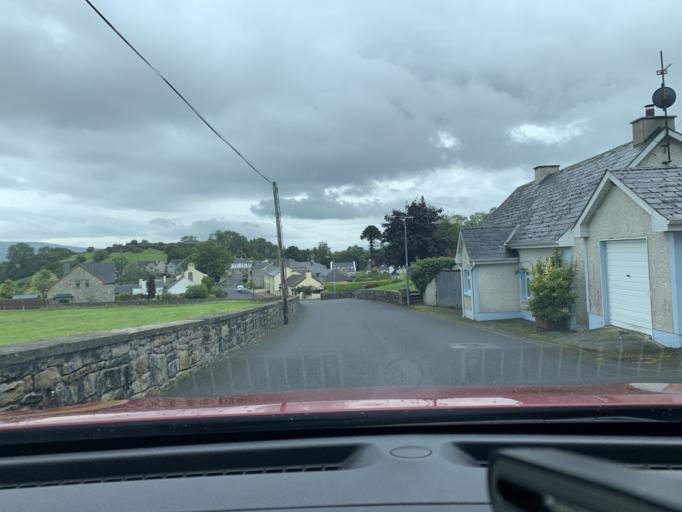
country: IE
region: Connaught
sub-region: County Leitrim
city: Manorhamilton
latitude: 54.3135
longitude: -8.2139
